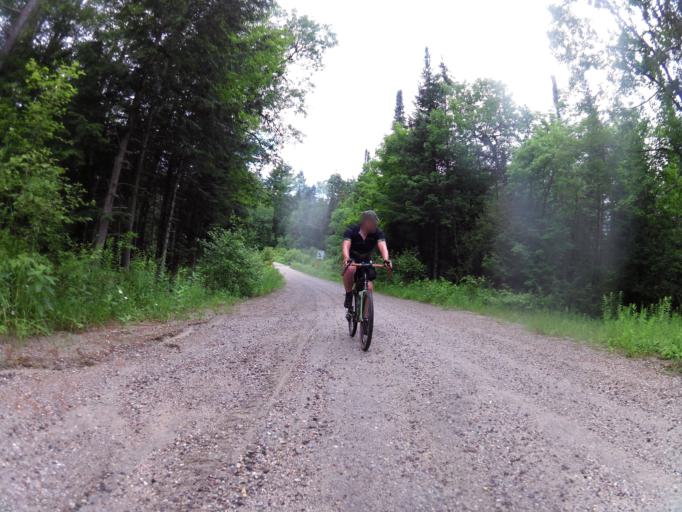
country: CA
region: Ontario
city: Renfrew
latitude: 45.0774
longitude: -76.7222
